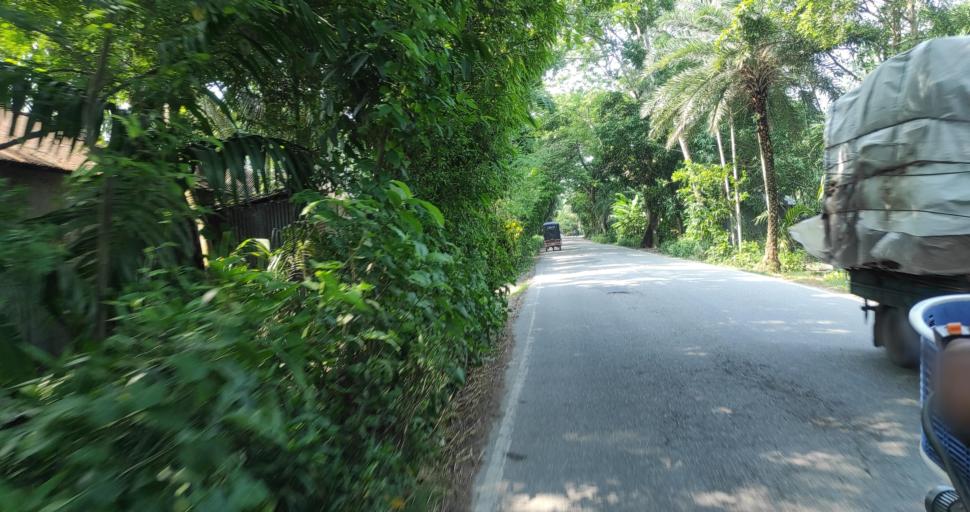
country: BD
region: Rajshahi
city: Ishurdi
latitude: 24.2854
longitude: 89.0653
